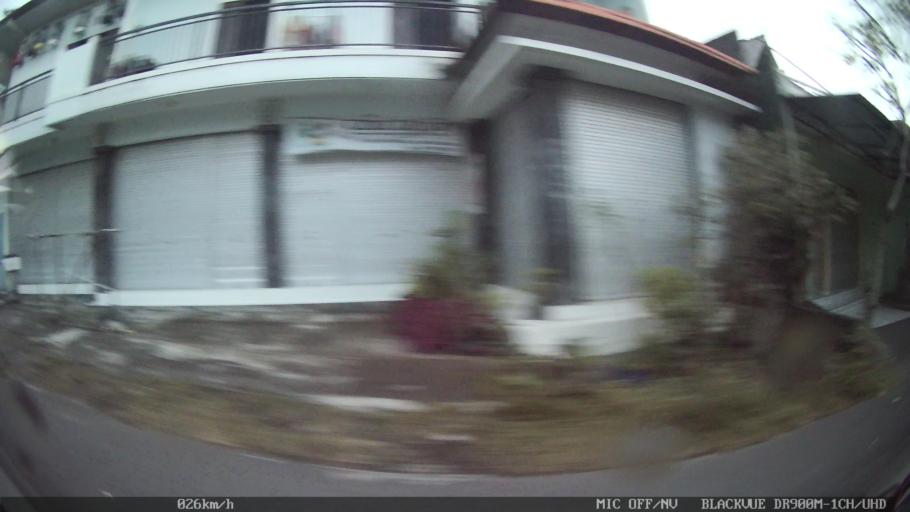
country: ID
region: Bali
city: Banjar Kertajiwa
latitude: -8.6397
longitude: 115.2710
